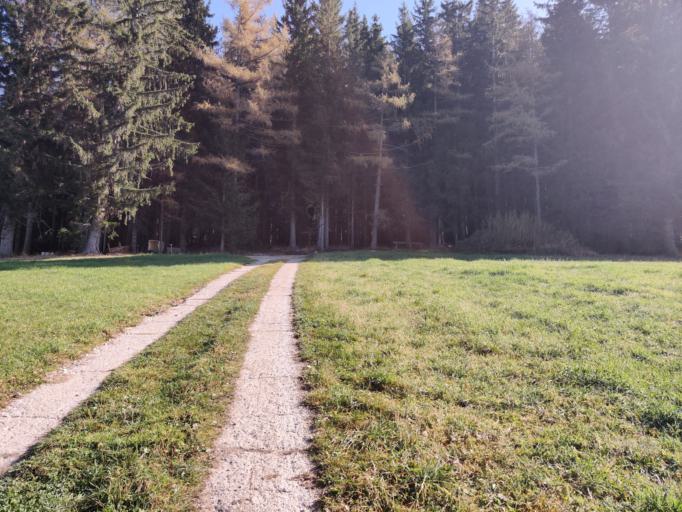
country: AT
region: Styria
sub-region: Politischer Bezirk Hartberg-Fuerstenfeld
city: Sankt Jakob im Walde
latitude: 47.4764
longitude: 15.8003
